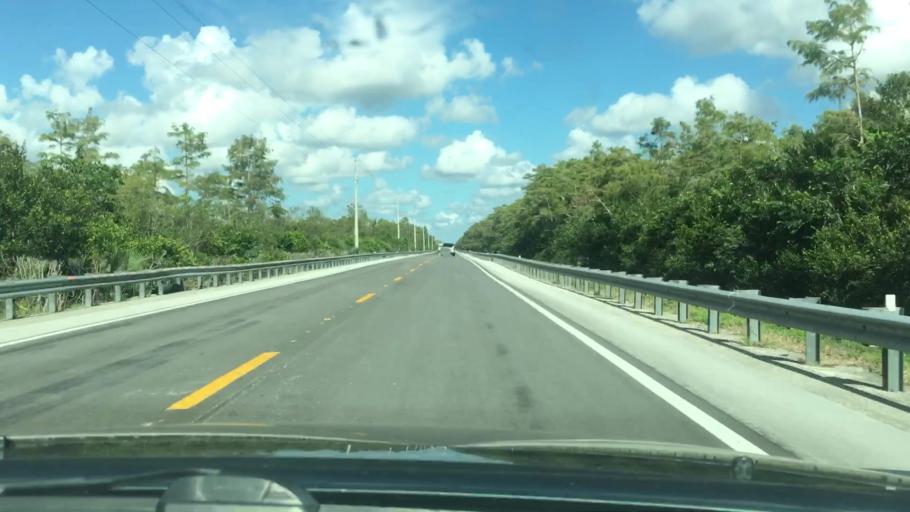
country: US
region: Florida
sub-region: Miami-Dade County
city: Kendall West
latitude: 25.7708
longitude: -80.8375
